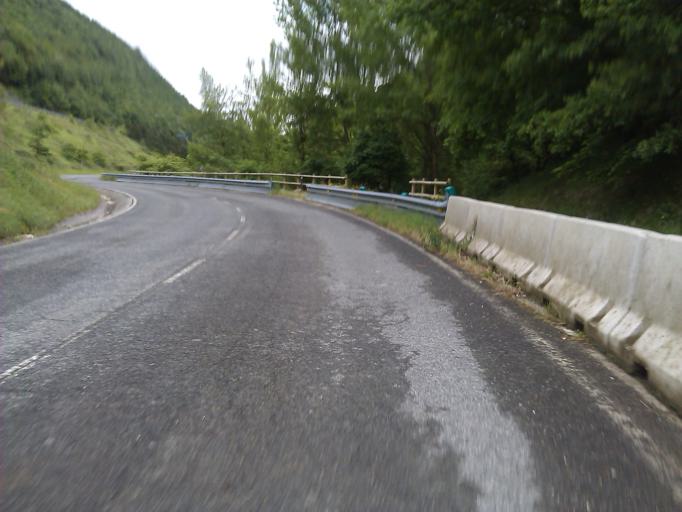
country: ES
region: Navarre
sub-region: Provincia de Navarra
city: Lekunberri
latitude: 42.9713
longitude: -1.8453
